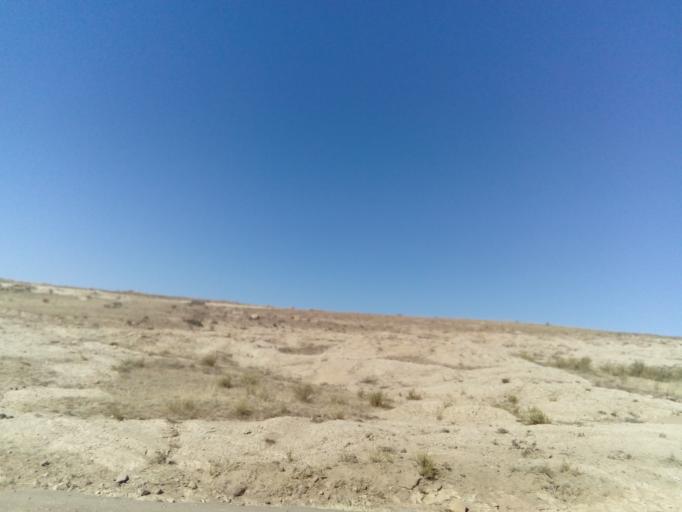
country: LS
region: Berea
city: Teyateyaneng
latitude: -29.1391
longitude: 27.8611
